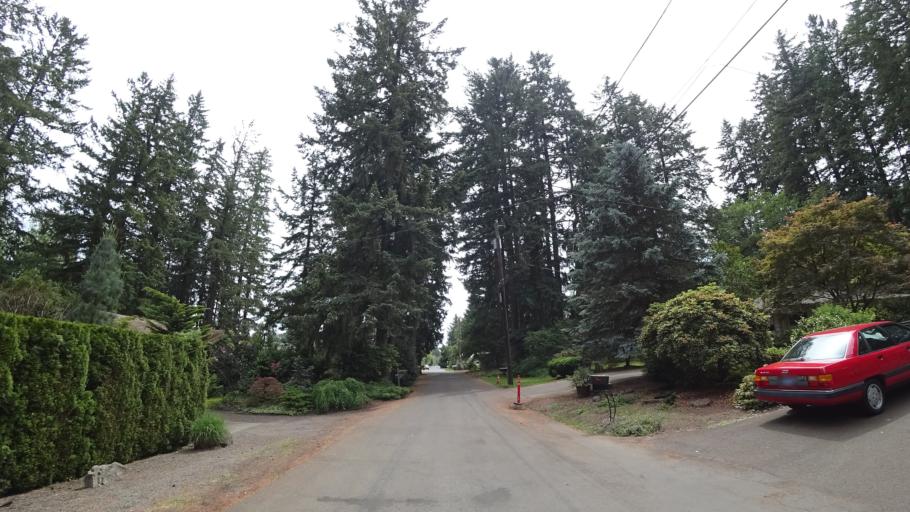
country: US
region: Oregon
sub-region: Washington County
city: Garden Home-Whitford
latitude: 45.4577
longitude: -122.7615
